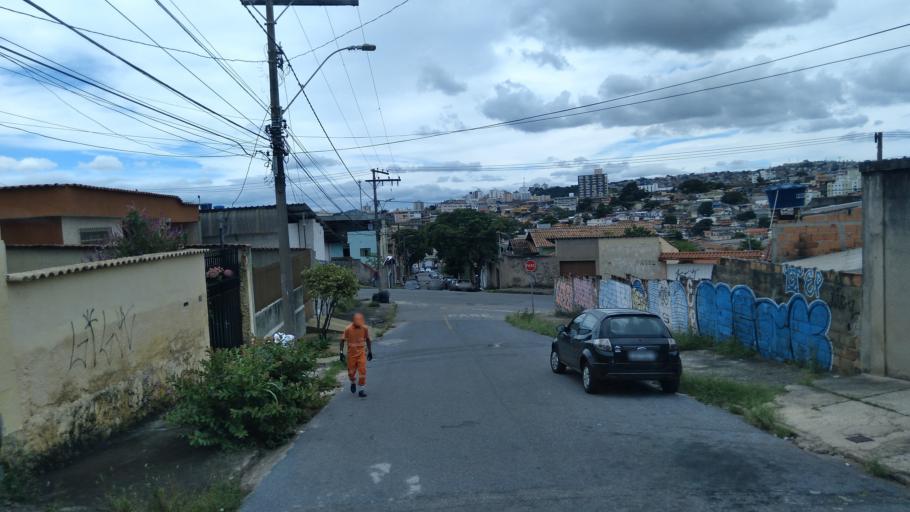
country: BR
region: Minas Gerais
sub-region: Contagem
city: Contagem
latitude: -19.9111
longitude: -44.0050
